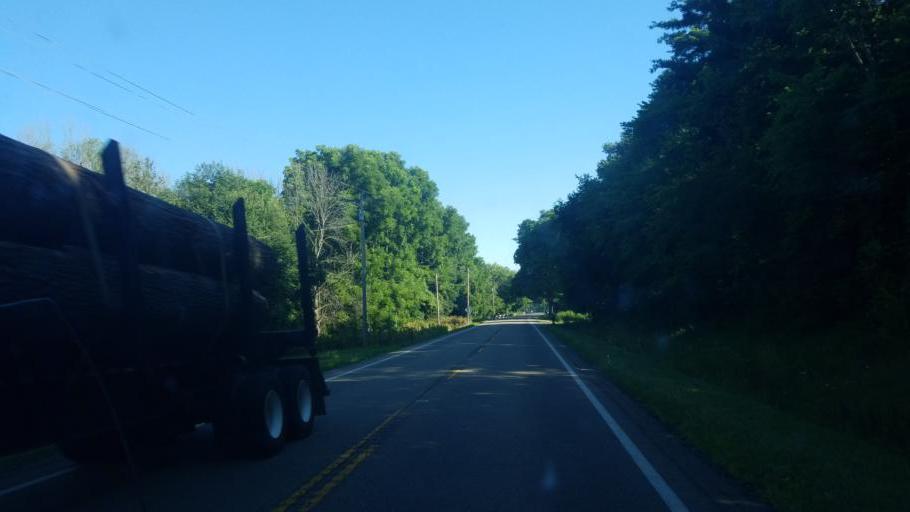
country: US
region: Ohio
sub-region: Wayne County
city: Shreve
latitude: 40.6549
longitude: -81.9406
